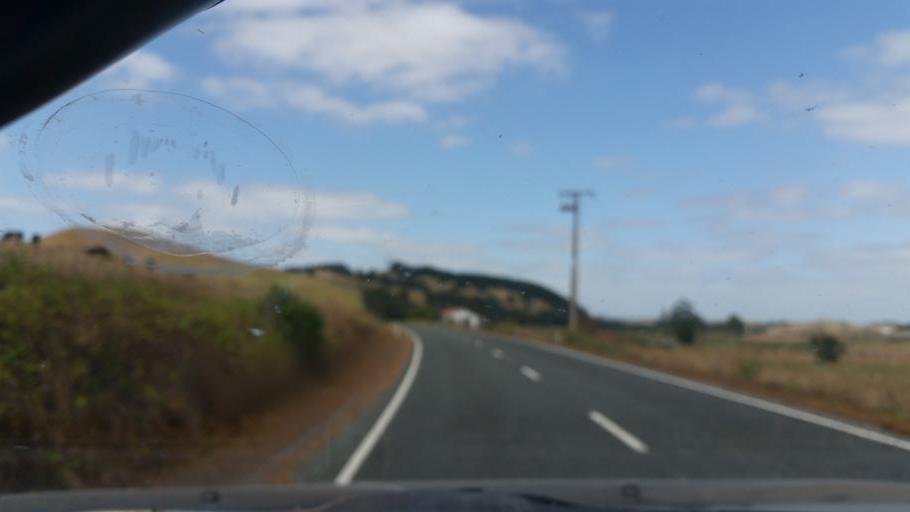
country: NZ
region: Northland
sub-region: Whangarei
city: Ruakaka
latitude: -35.9617
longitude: 174.2907
